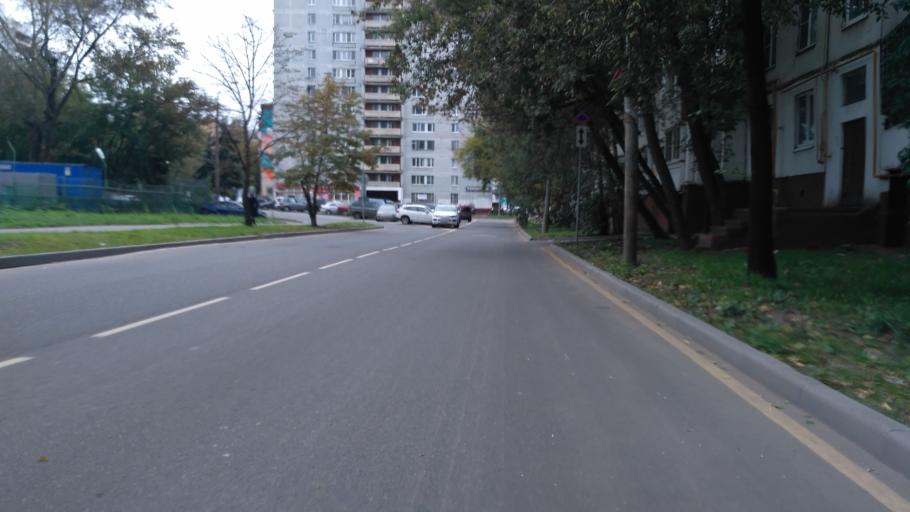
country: RU
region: Moscow
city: Mar'ina Roshcha
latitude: 55.7973
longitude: 37.6083
